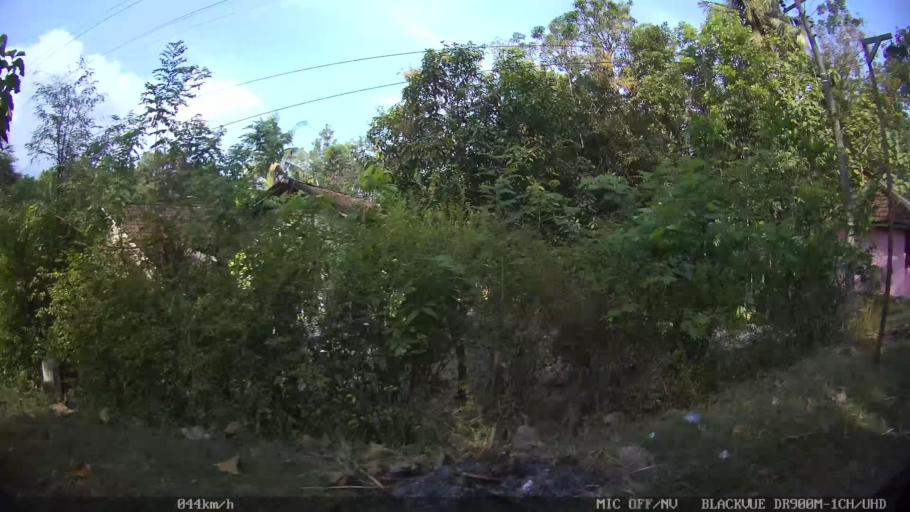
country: ID
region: Daerah Istimewa Yogyakarta
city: Kasihan
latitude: -7.8566
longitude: 110.3194
